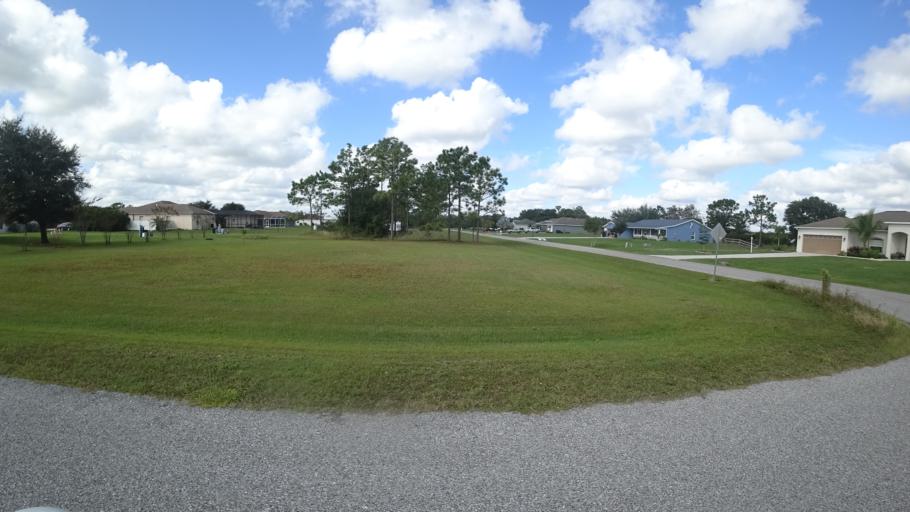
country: US
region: Florida
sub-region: Sarasota County
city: Lake Sarasota
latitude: 27.3929
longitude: -82.2722
